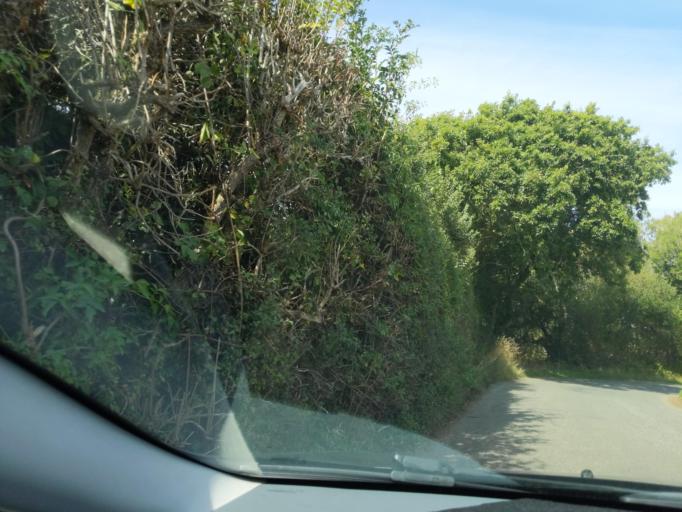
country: GB
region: England
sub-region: Cornwall
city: Torpoint
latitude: 50.3585
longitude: -4.2326
